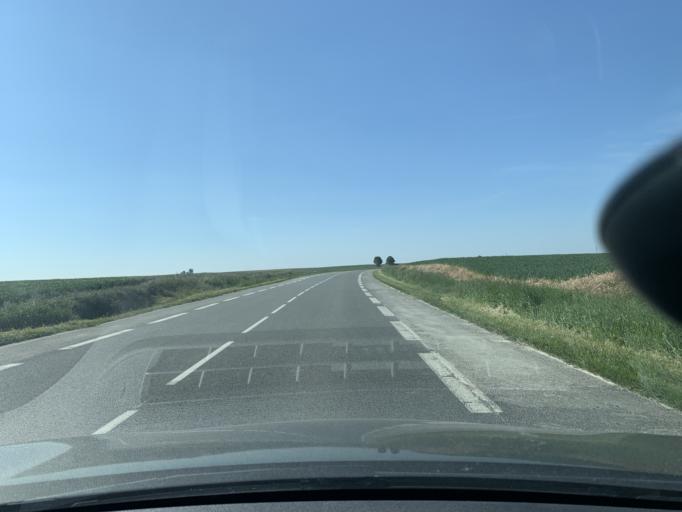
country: FR
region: Nord-Pas-de-Calais
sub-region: Departement du Nord
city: Rumilly-en-Cambresis
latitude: 50.1324
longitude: 3.2460
